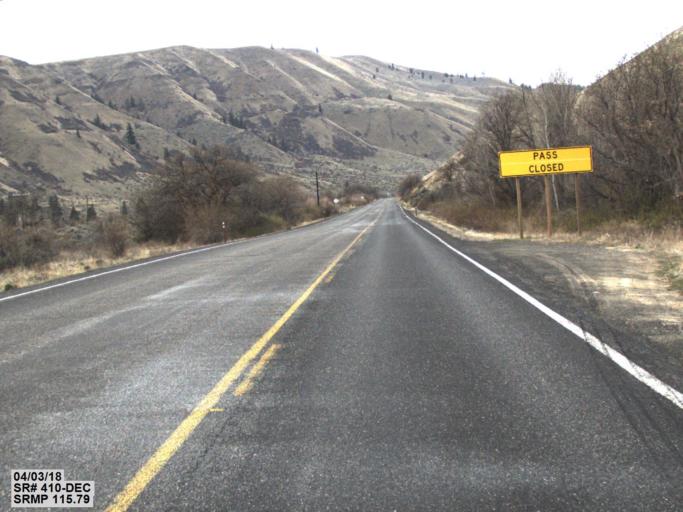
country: US
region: Washington
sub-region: Yakima County
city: Tieton
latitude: 46.7488
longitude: -120.8007
